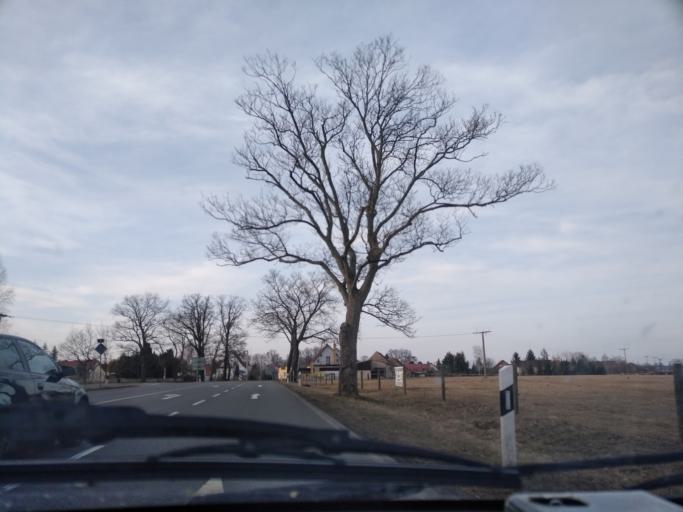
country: DE
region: Saxony-Anhalt
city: Holzdorf
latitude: 51.7950
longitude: 13.1800
